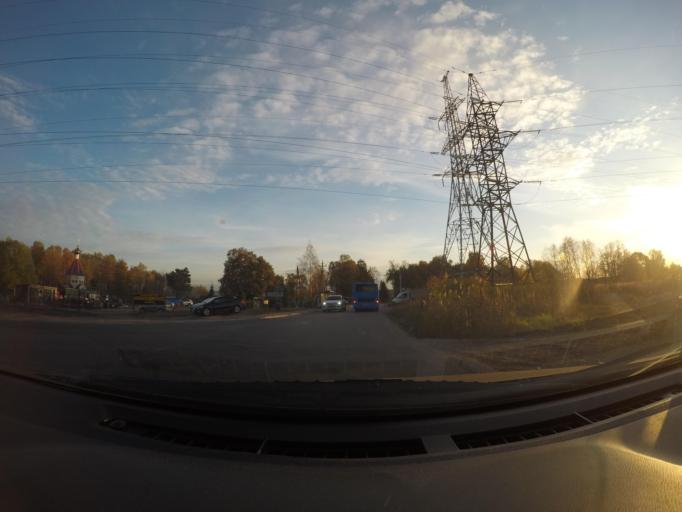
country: RU
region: Moskovskaya
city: Firsanovka
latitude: 55.9388
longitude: 37.2492
